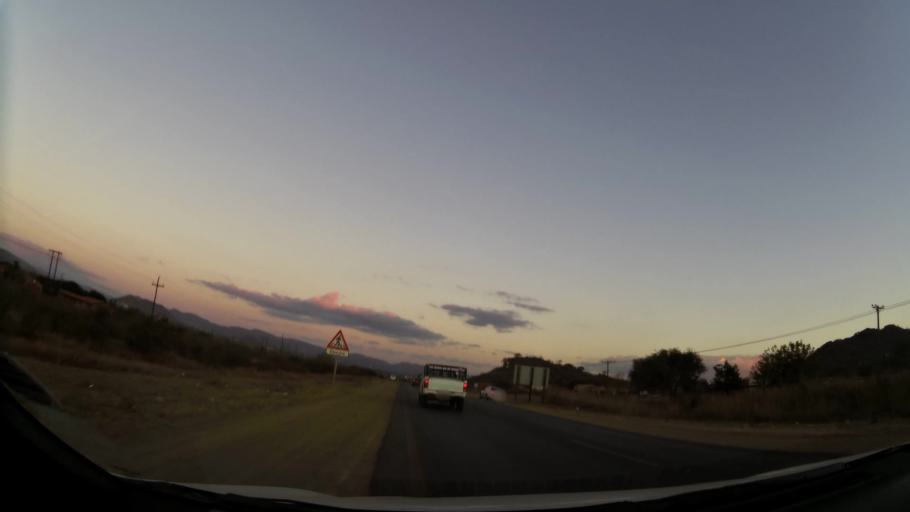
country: ZA
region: Limpopo
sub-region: Waterberg District Municipality
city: Mokopane
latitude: -24.1526
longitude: 28.9762
